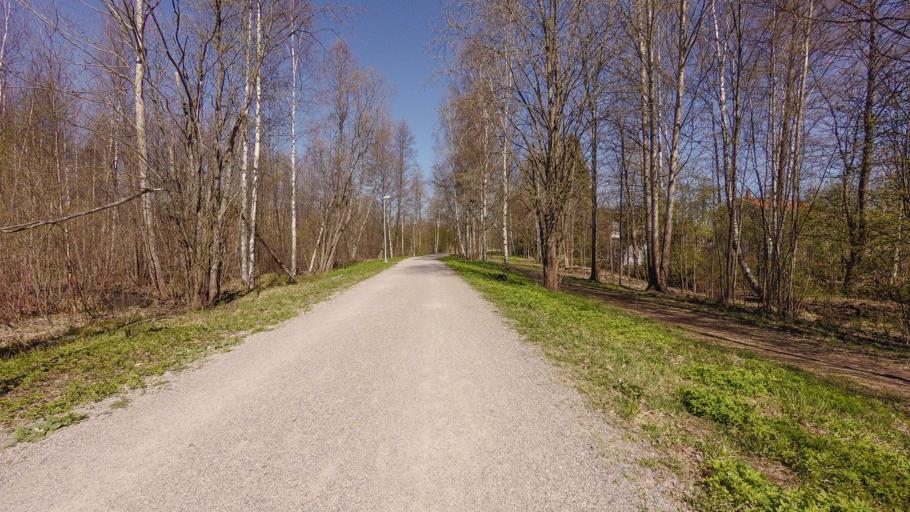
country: FI
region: Uusimaa
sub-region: Helsinki
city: Vantaa
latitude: 60.2253
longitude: 25.0907
